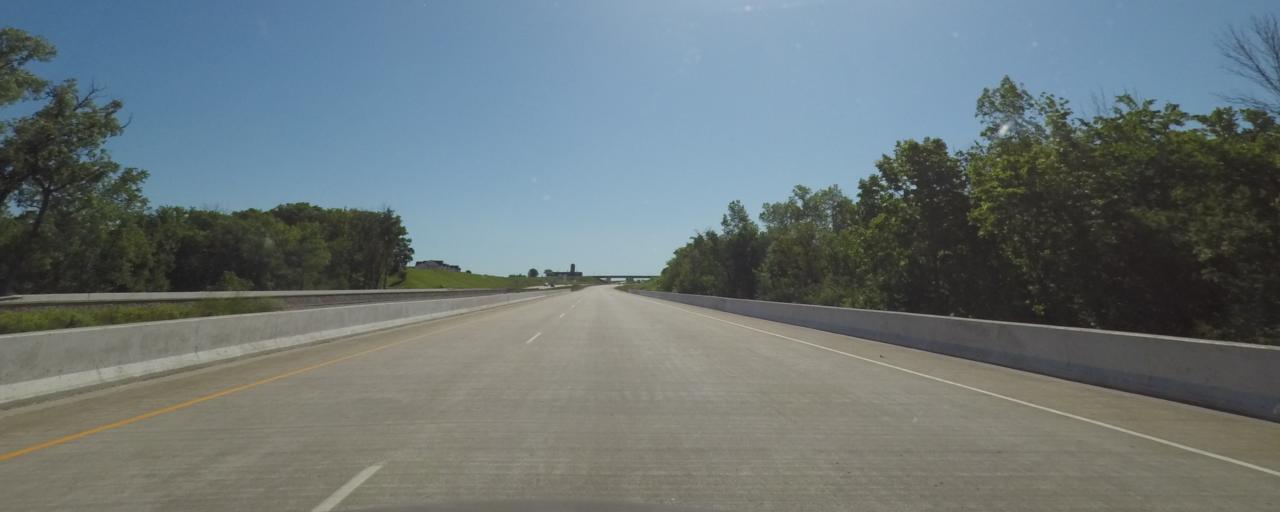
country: US
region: Wisconsin
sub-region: Fond du Lac County
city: Fond du Lac
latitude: 43.7367
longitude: -88.4594
